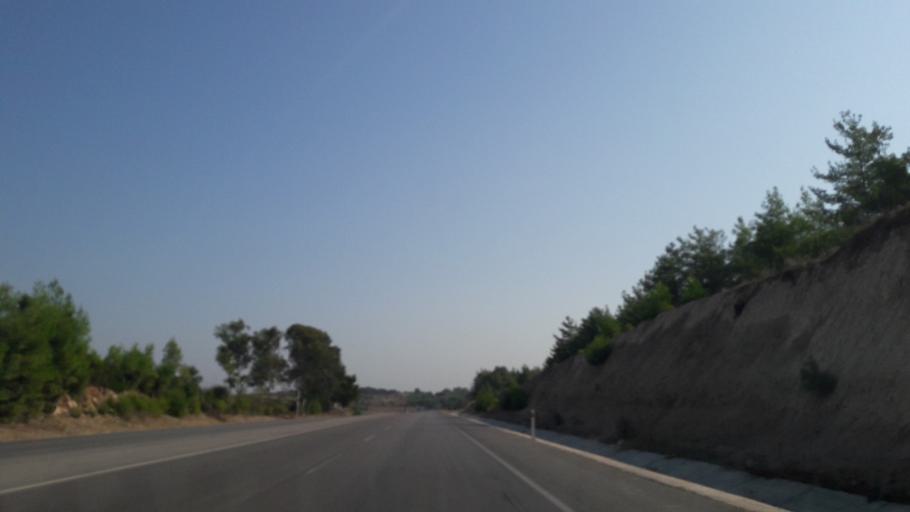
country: TR
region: Adana
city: Sagkaya
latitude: 37.1571
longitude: 35.5510
